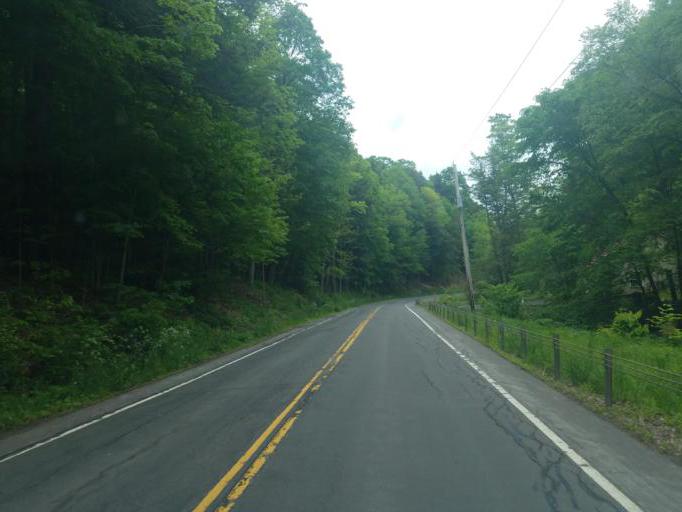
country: US
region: New York
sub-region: Herkimer County
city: Frankfort
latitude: 42.9417
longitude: -75.1138
